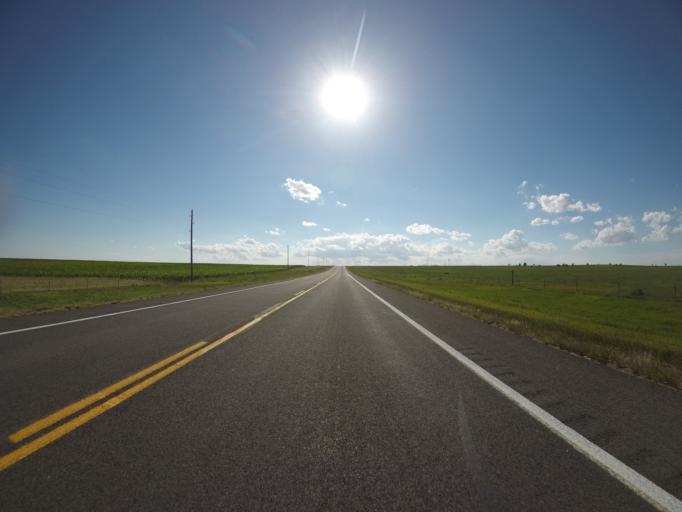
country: US
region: Colorado
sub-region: Morgan County
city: Fort Morgan
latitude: 40.6108
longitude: -103.7573
